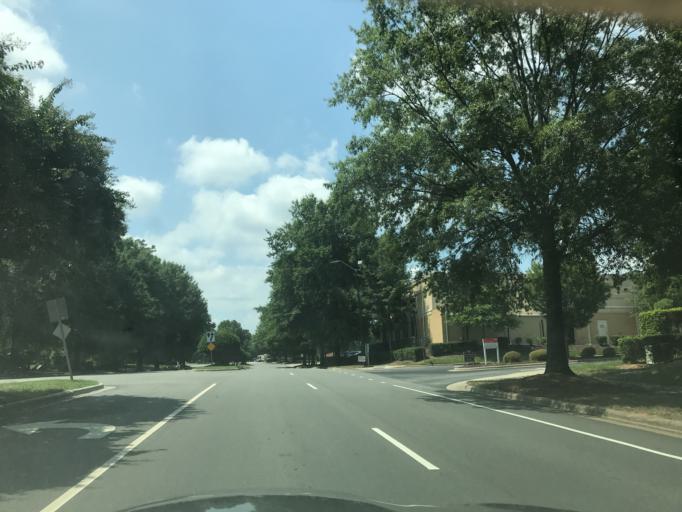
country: US
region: North Carolina
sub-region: Wake County
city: Wake Forest
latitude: 35.9079
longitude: -78.5875
